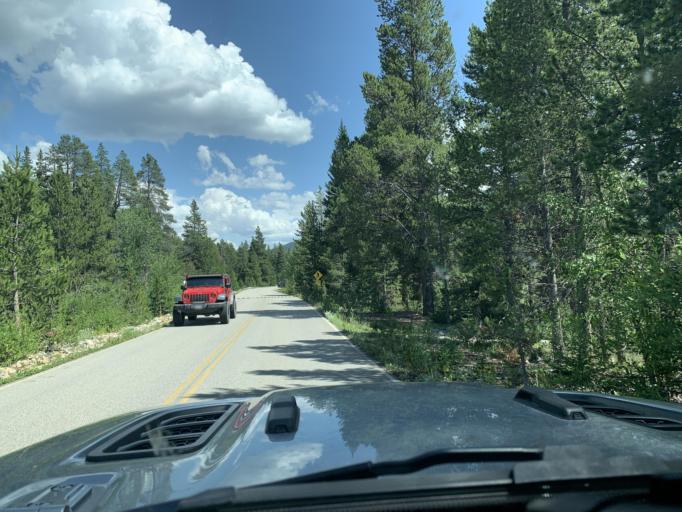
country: US
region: Colorado
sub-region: Lake County
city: Leadville North
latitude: 39.2797
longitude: -106.4365
